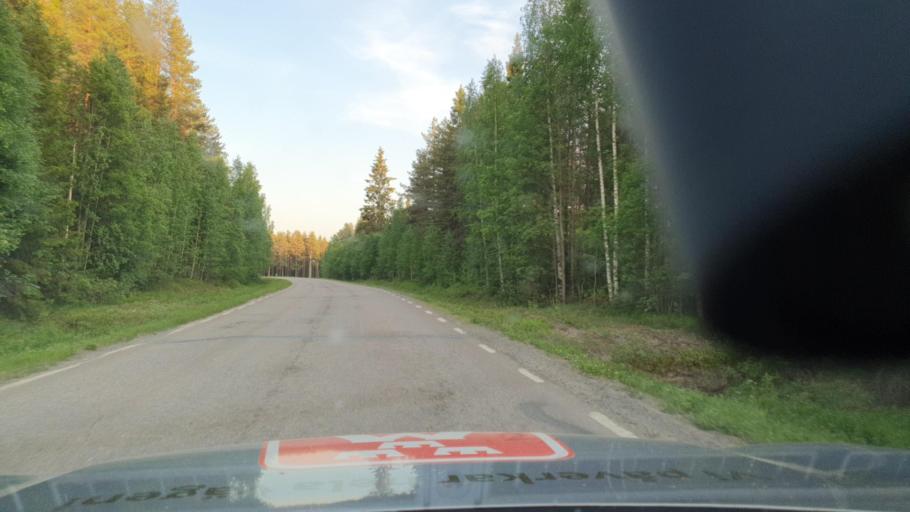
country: SE
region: Norrbotten
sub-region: Bodens Kommun
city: Boden
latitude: 66.0499
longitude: 21.7851
